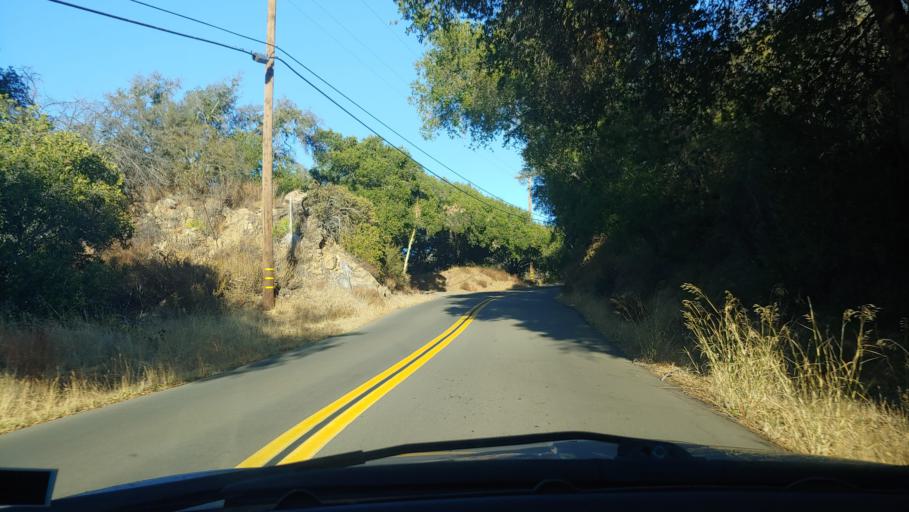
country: US
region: California
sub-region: Santa Barbara County
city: Goleta
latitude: 34.5357
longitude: -119.8494
